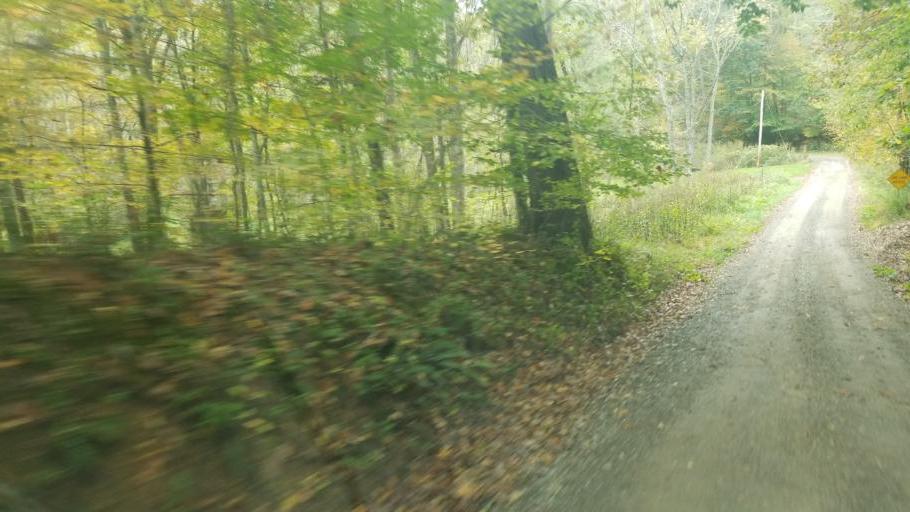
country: US
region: Ohio
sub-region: Holmes County
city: Millersburg
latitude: 40.5361
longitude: -82.0503
